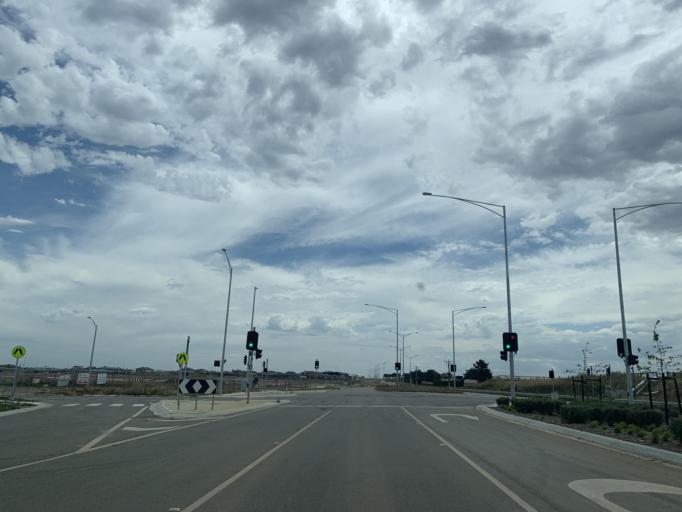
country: AU
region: Victoria
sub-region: Cardinia
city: Officer South
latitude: -38.1235
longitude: 145.3656
